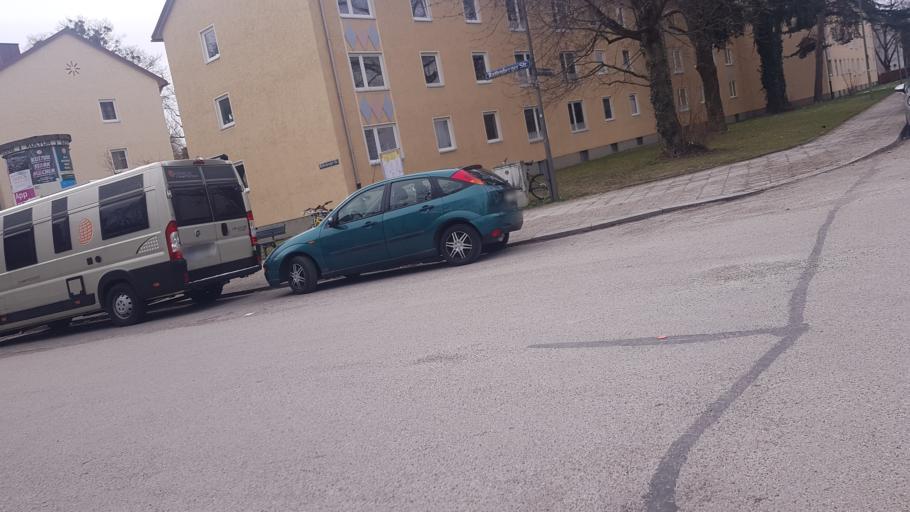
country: DE
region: Bavaria
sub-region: Upper Bavaria
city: Munich
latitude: 48.1214
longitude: 11.5271
